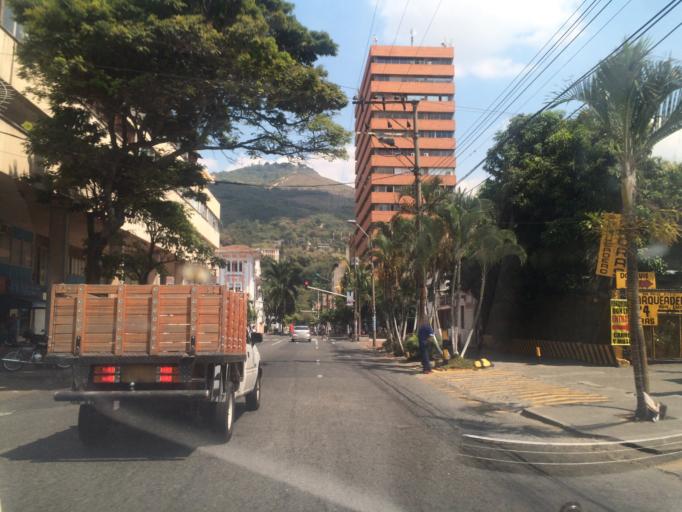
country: CO
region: Valle del Cauca
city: Cali
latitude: 3.4579
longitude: -76.5323
